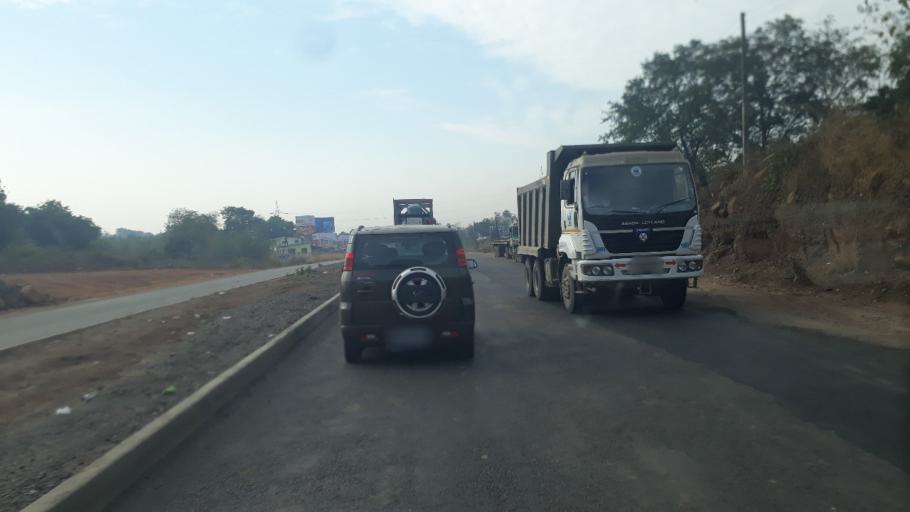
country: IN
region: Maharashtra
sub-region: Raigarh
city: Pen
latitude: 18.8210
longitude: 73.0922
